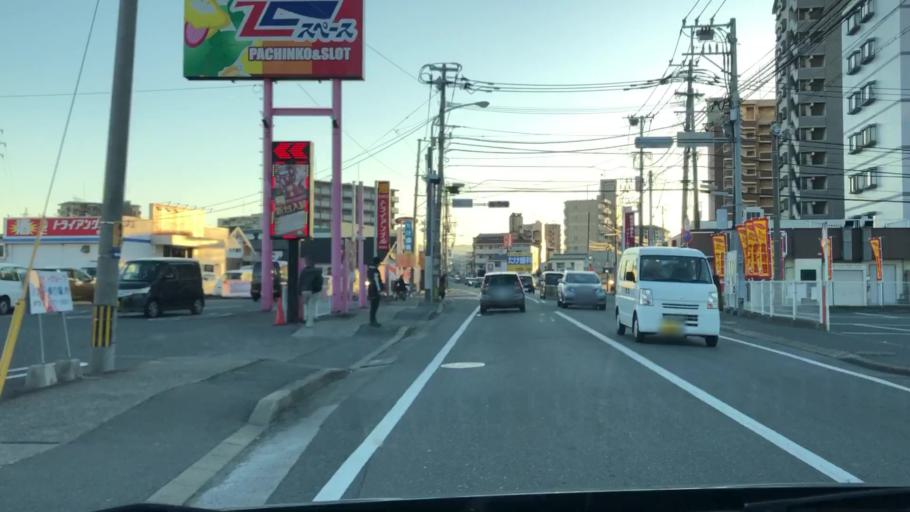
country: JP
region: Fukuoka
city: Fukuoka-shi
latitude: 33.6229
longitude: 130.4378
